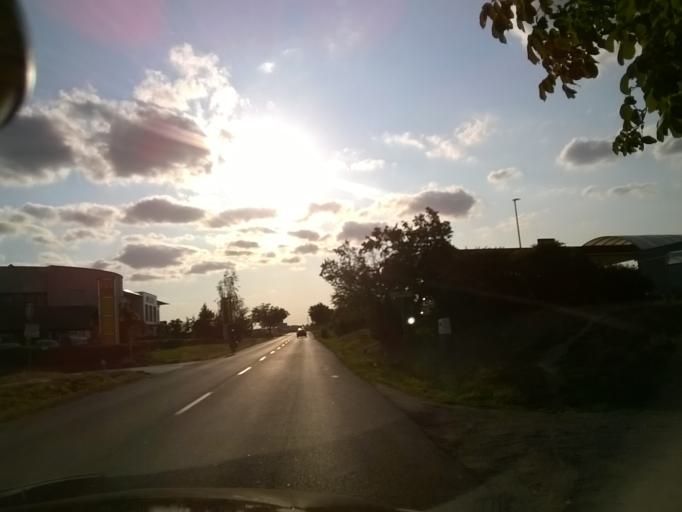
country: SK
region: Nitriansky
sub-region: Okres Nitra
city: Nitra
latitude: 48.3156
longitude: 18.0306
